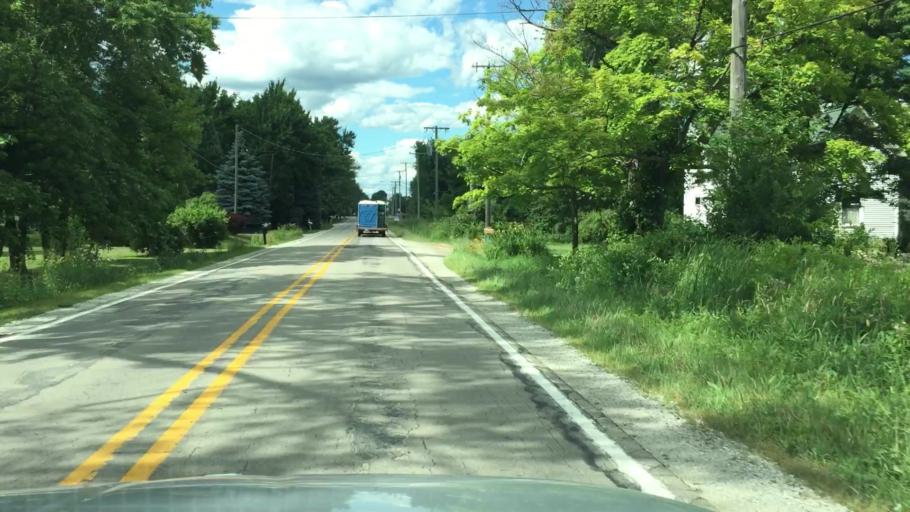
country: US
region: Michigan
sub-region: Saint Clair County
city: Capac
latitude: 42.9210
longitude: -82.9455
